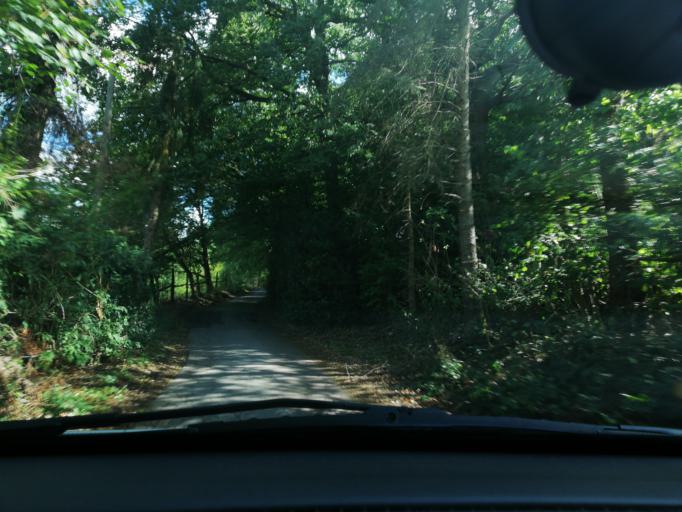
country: DE
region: North Rhine-Westphalia
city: Wetter (Ruhr)
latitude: 51.3783
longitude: 7.3592
